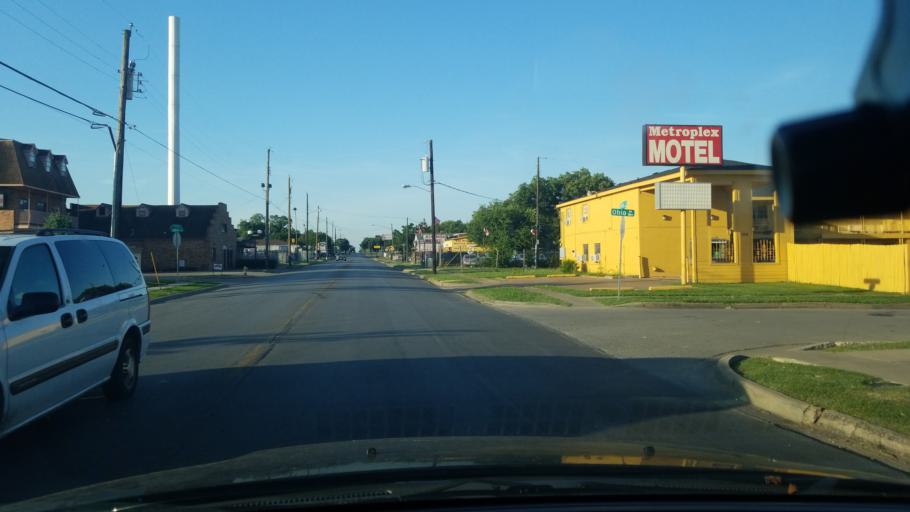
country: US
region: Texas
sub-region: Dallas County
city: Dallas
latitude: 32.7197
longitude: -96.8229
